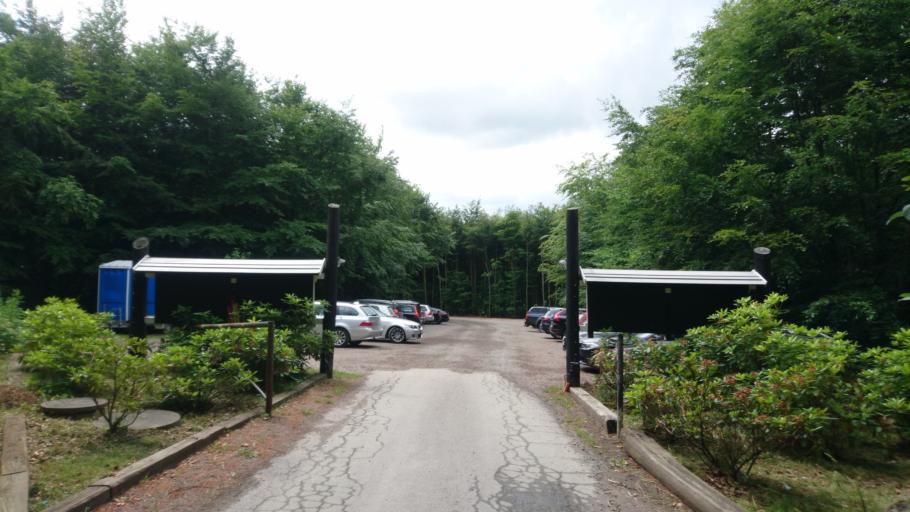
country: SE
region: Skane
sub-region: Lunds Kommun
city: Veberod
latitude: 55.6348
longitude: 13.4309
